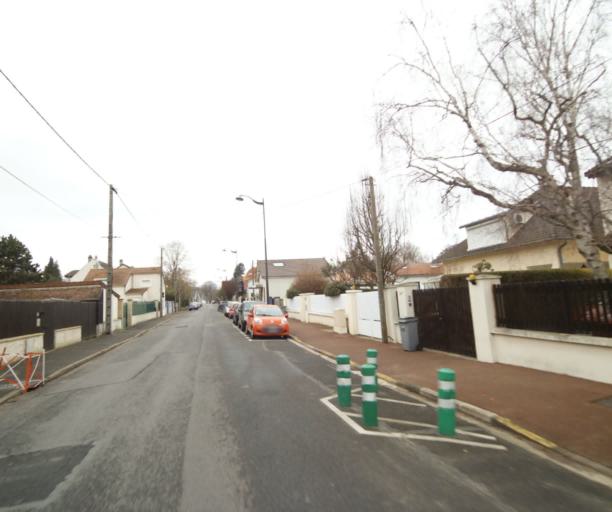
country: FR
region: Ile-de-France
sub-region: Departement des Hauts-de-Seine
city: Garches
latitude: 48.8576
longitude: 2.1876
